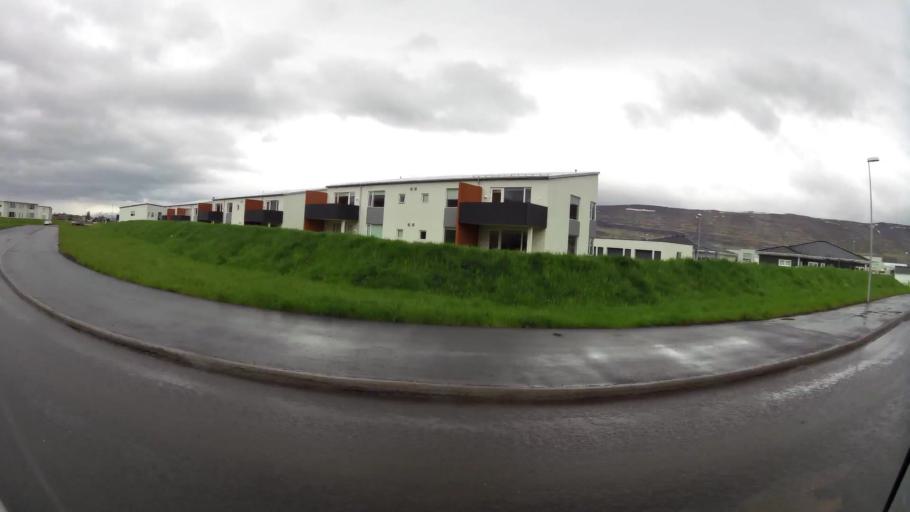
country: IS
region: Northeast
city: Akureyri
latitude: 65.6663
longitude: -18.1072
